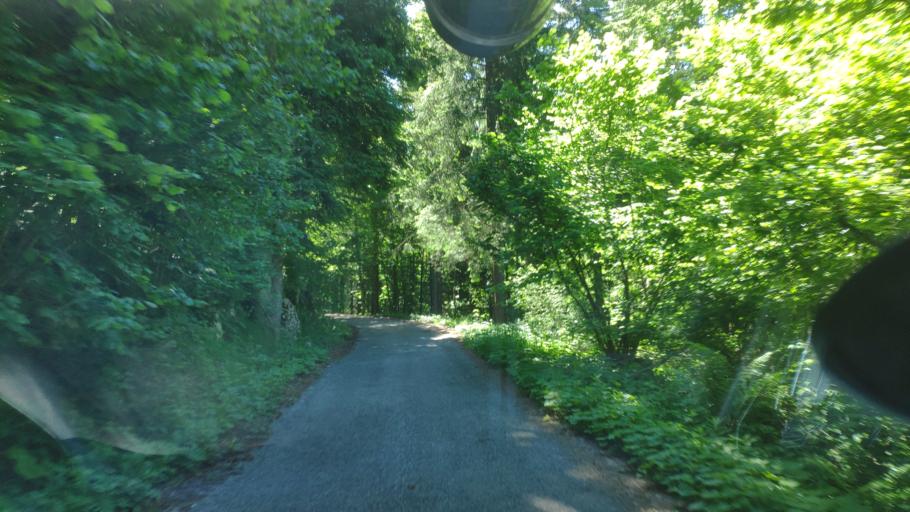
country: IT
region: Veneto
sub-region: Provincia di Vicenza
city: Cogollo del Cengio
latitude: 45.8228
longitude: 11.4437
